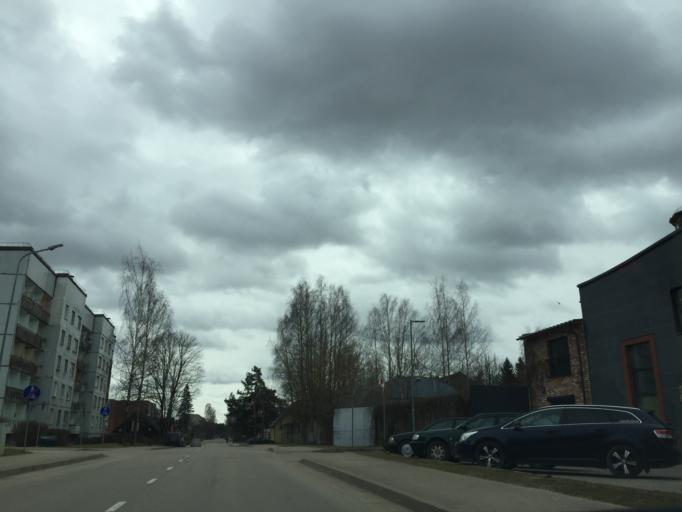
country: LV
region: Livani
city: Livani
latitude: 56.3526
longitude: 26.1736
